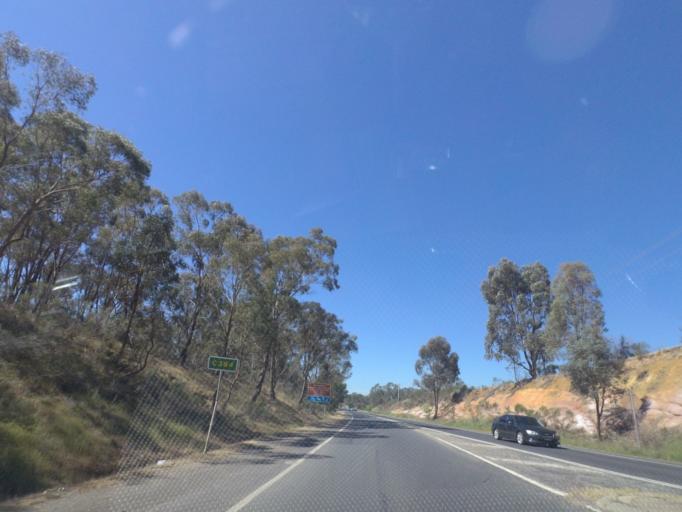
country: AU
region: Victoria
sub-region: Murrindindi
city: Kinglake West
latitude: -37.0291
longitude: 145.1059
